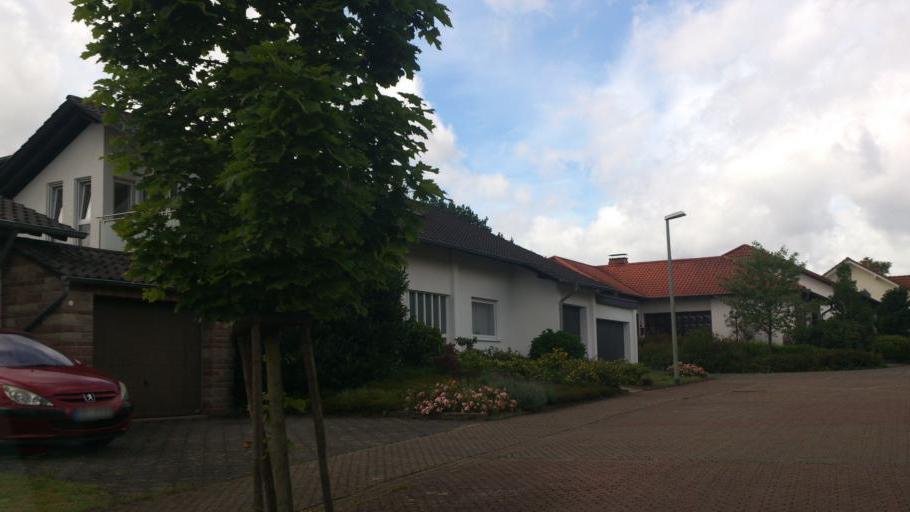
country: DE
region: Saarland
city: Tholey
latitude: 49.4961
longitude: 6.9792
